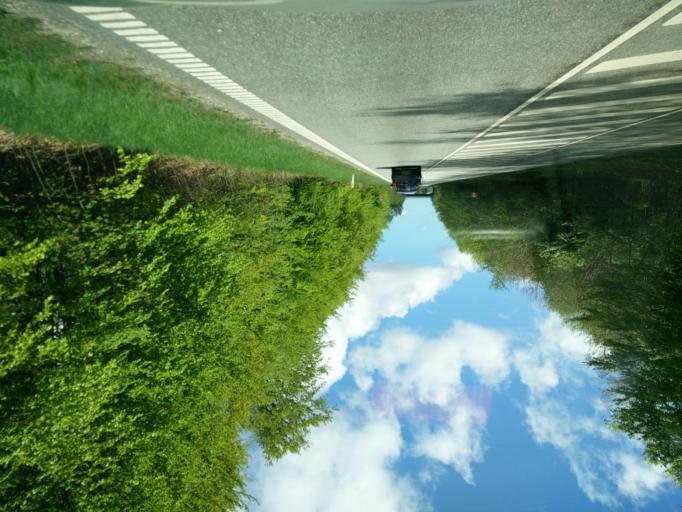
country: DK
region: Capital Region
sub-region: Hillerod Kommune
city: Hillerod
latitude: 55.8872
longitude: 12.2962
